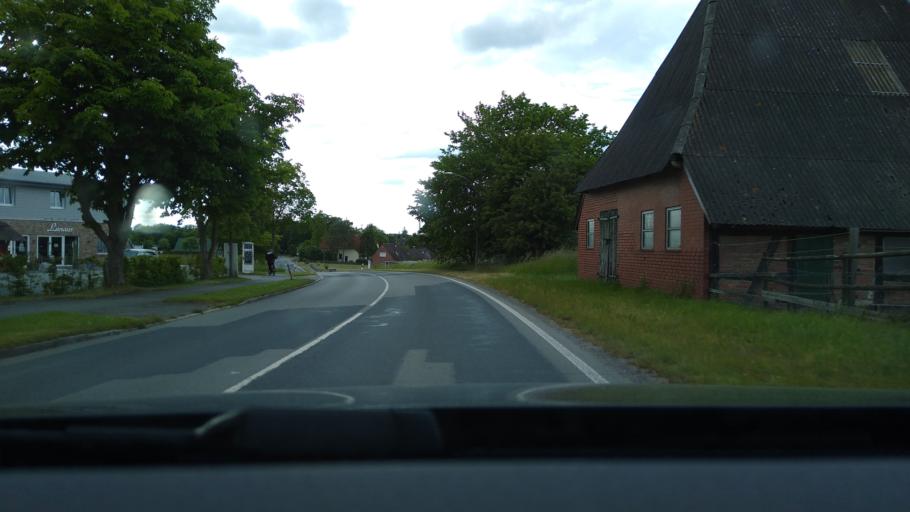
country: DE
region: Schleswig-Holstein
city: Kabelhorst
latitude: 54.2135
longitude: 10.9257
